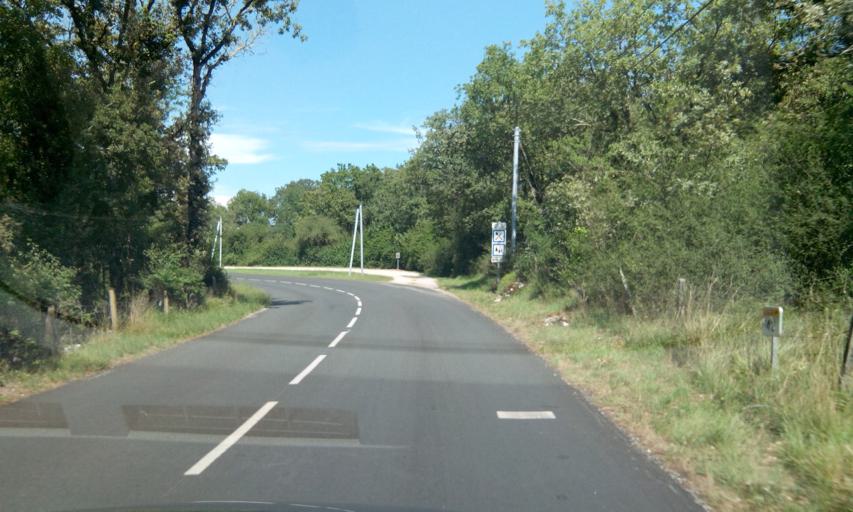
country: FR
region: Midi-Pyrenees
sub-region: Departement du Lot
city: Gramat
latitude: 44.8109
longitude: 1.6377
